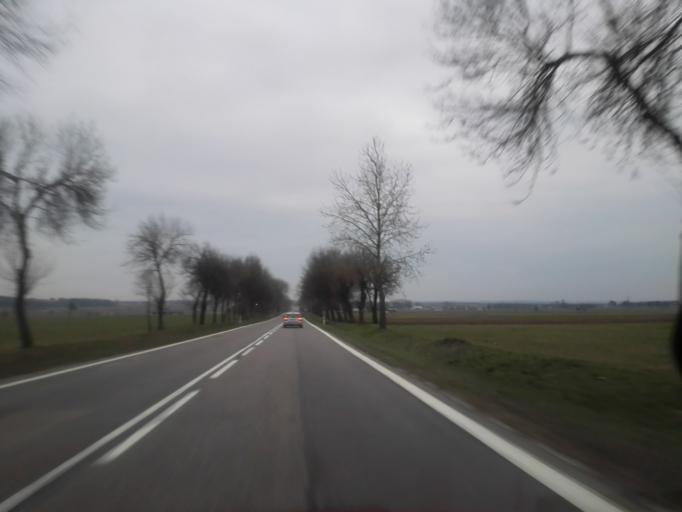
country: PL
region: Podlasie
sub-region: Powiat lomzynski
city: Piatnica
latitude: 53.2663
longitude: 22.1287
